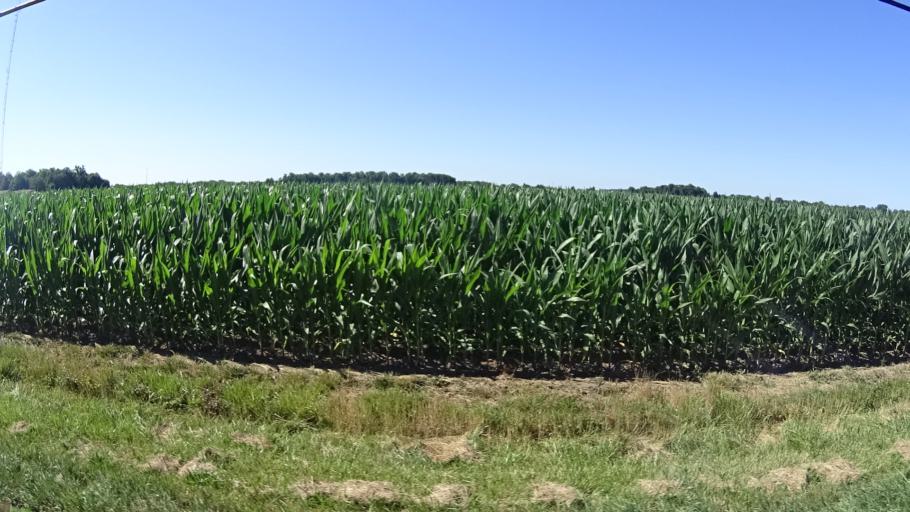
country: US
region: Ohio
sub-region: Erie County
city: Sandusky
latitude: 41.4091
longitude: -82.7168
